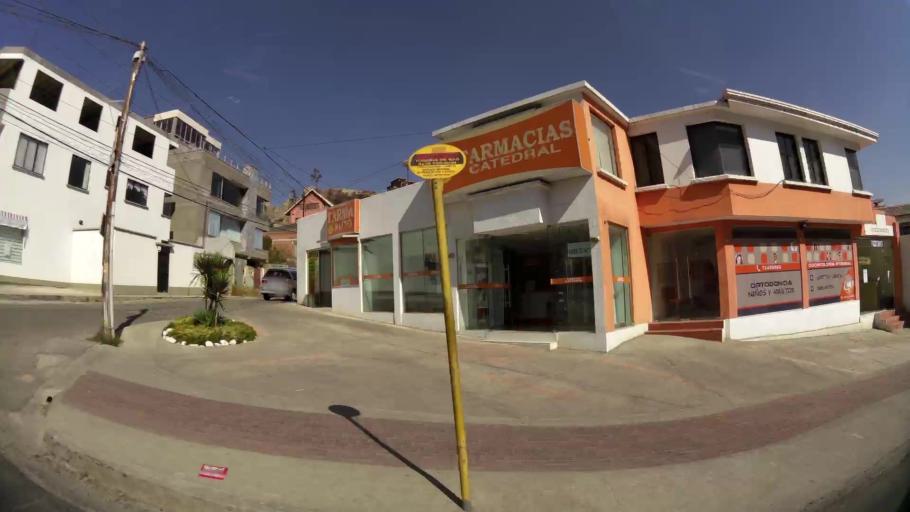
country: BO
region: La Paz
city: La Paz
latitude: -16.5222
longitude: -68.0650
